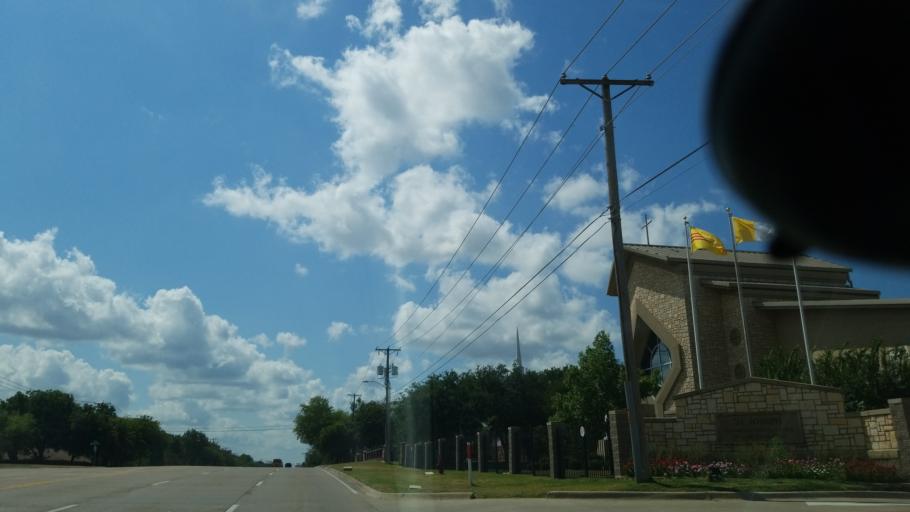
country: US
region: Texas
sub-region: Dallas County
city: Grand Prairie
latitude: 32.7188
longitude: -96.9942
